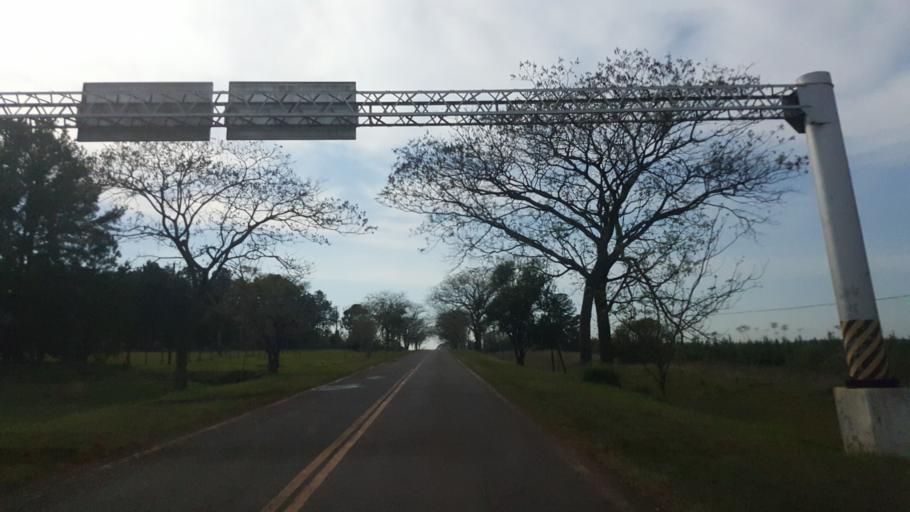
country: AR
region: Misiones
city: Capiovi
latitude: -26.9334
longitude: -55.1096
